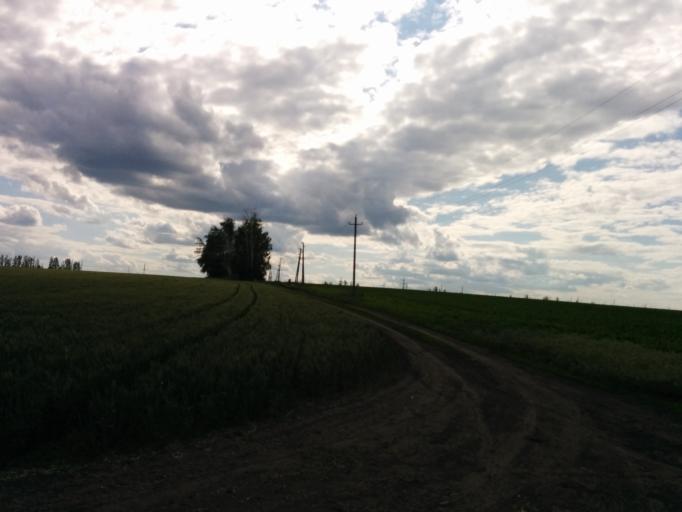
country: RU
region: Tambov
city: Donskoye
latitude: 52.7987
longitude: 41.4263
